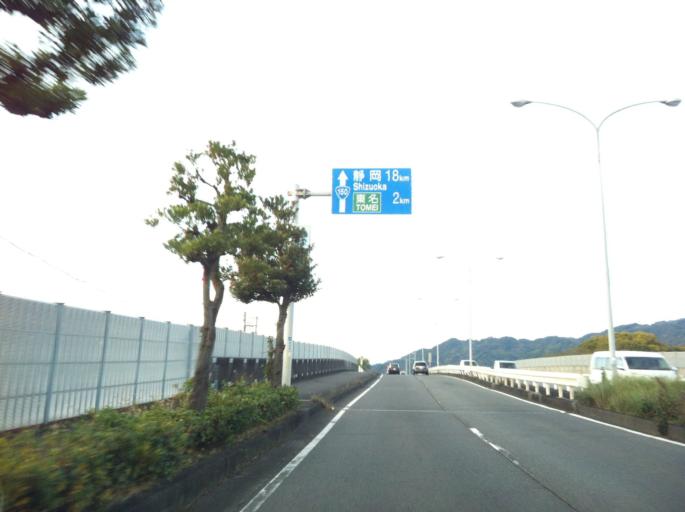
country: JP
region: Shizuoka
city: Yaizu
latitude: 34.8702
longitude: 138.2994
